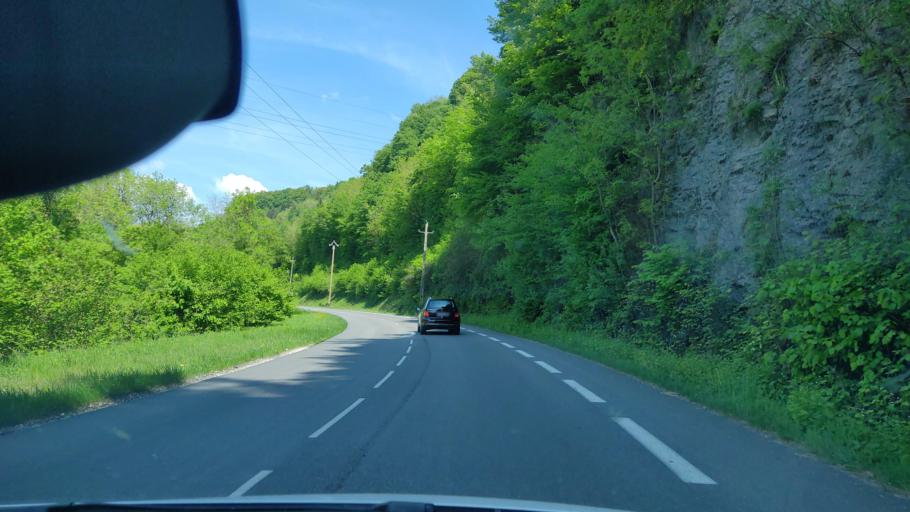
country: FR
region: Rhone-Alpes
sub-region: Departement de la Savoie
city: La Bridoire
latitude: 45.5333
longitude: 5.7486
